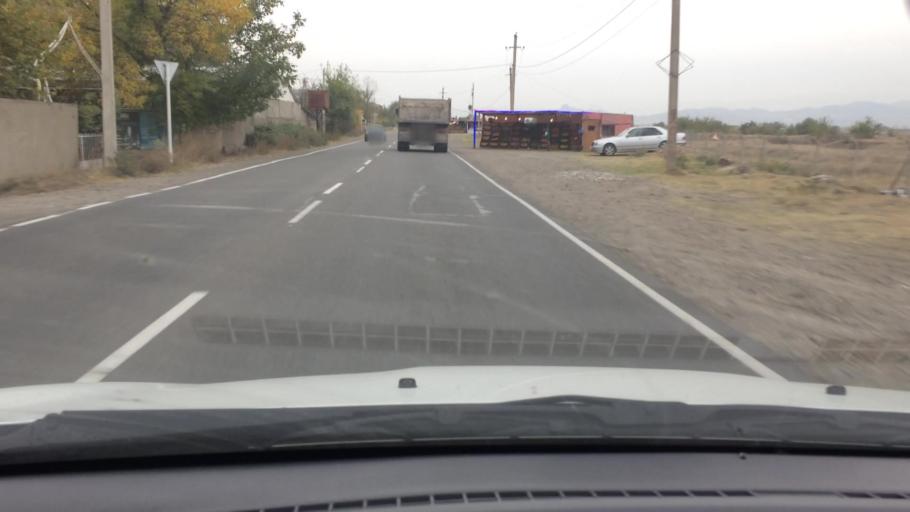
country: GE
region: Kvemo Kartli
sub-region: Marneuli
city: Marneuli
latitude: 41.4756
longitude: 44.8035
